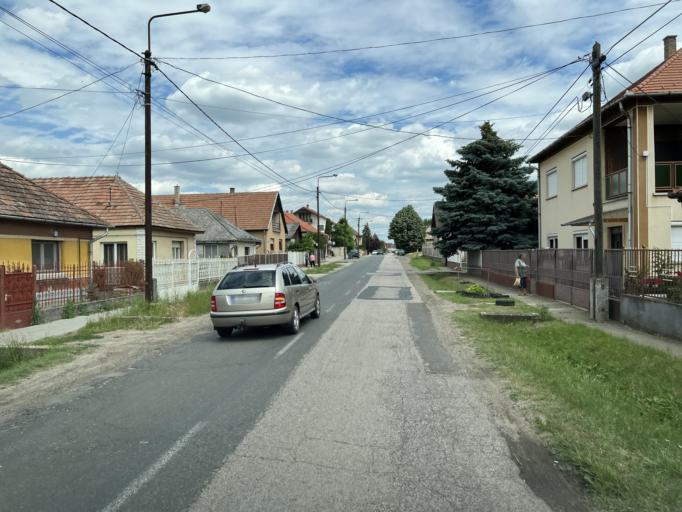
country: HU
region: Pest
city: Toalmas
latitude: 47.5076
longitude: 19.6629
